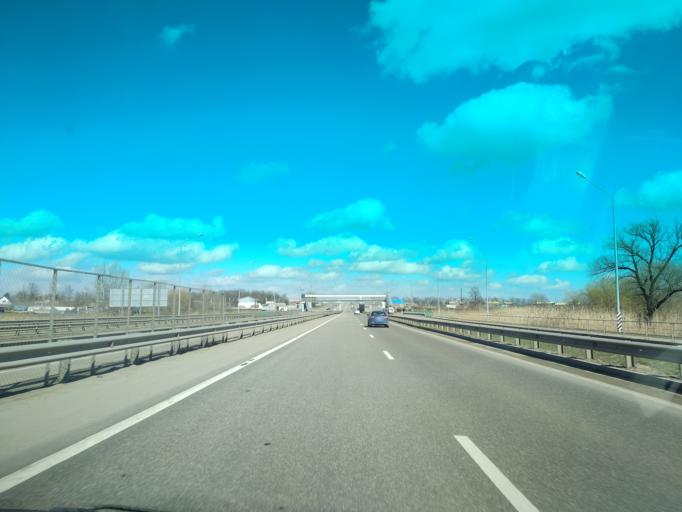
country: RU
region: Krasnodarskiy
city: Korenovsk
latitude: 45.5733
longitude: 39.5024
